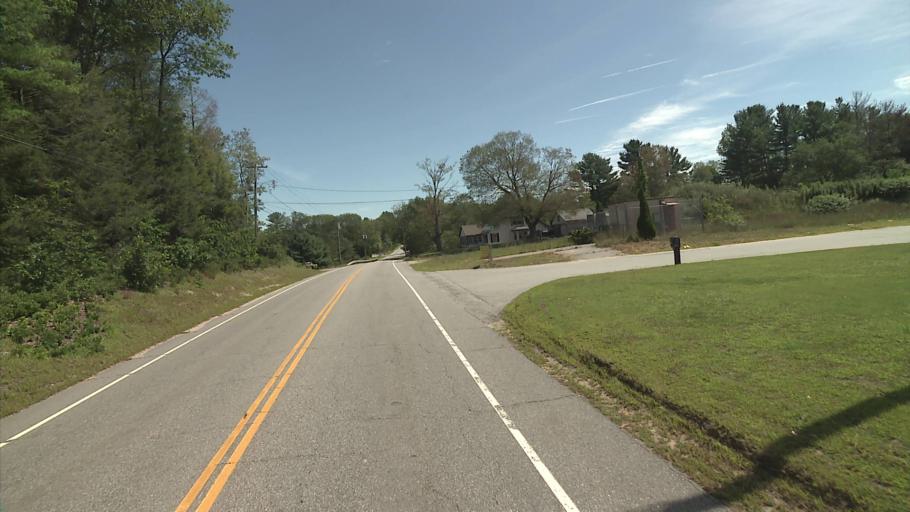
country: US
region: Connecticut
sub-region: Windham County
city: Killingly Center
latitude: 41.8483
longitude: -71.9285
